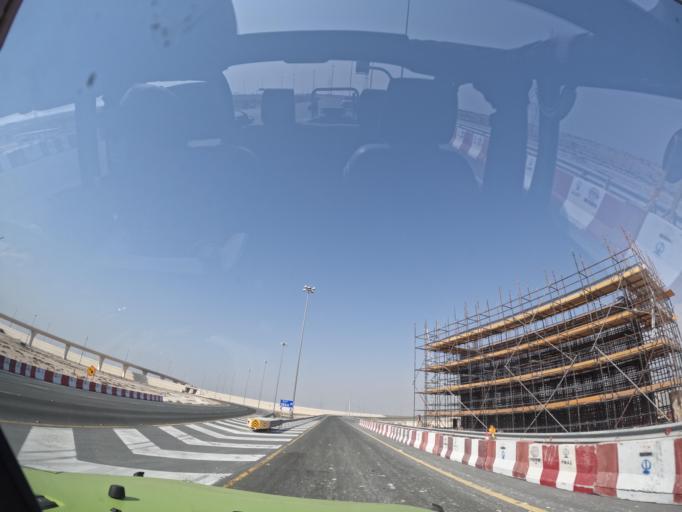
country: AE
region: Abu Dhabi
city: Abu Dhabi
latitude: 24.6747
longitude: 54.8220
